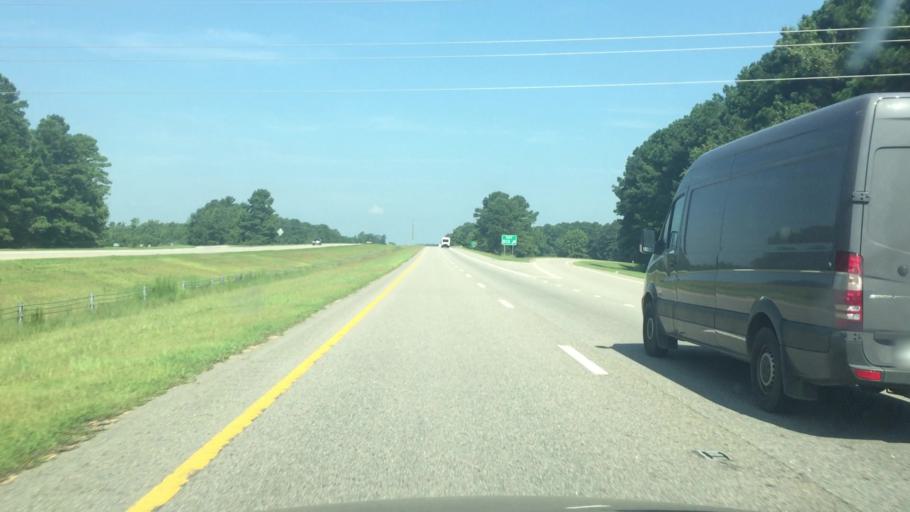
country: US
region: North Carolina
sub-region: Robeson County
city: Lumberton
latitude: 34.5777
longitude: -79.0442
